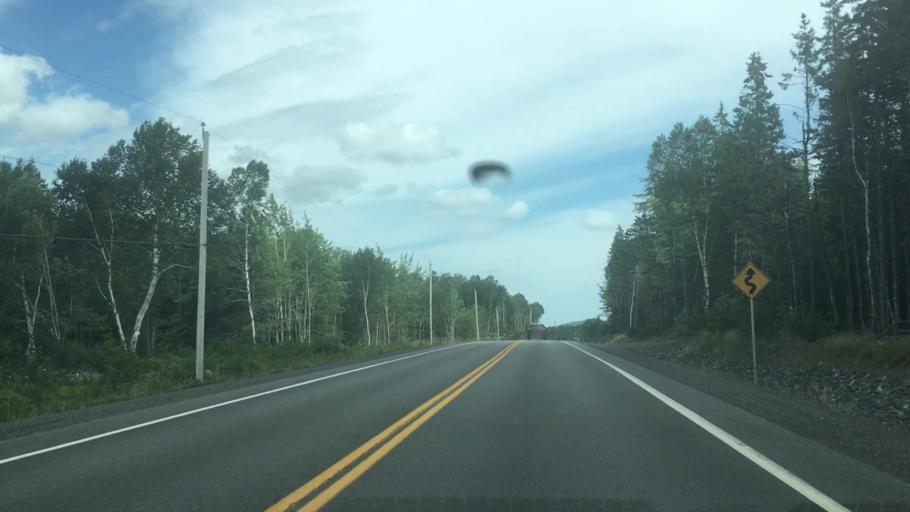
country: CA
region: Nova Scotia
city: Sydney Mines
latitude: 46.3132
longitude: -60.6134
